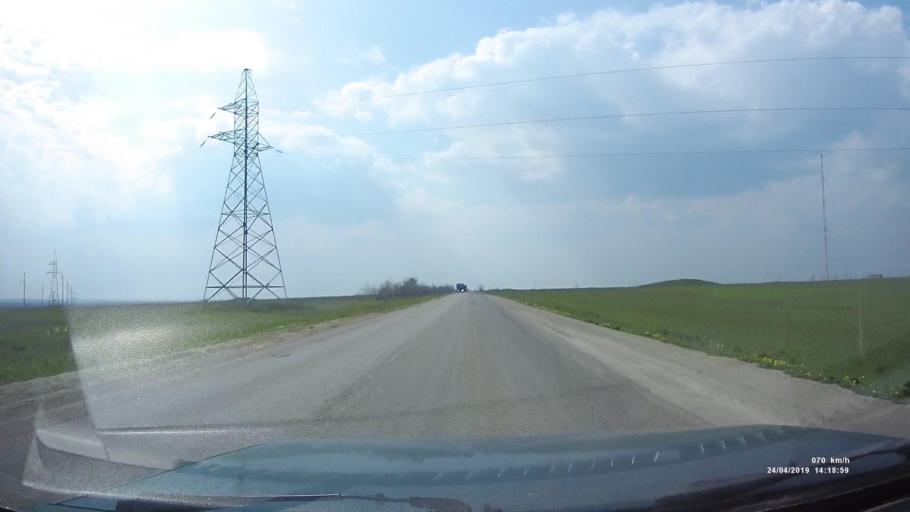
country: RU
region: Kalmykiya
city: Arshan'
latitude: 46.3041
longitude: 44.1834
